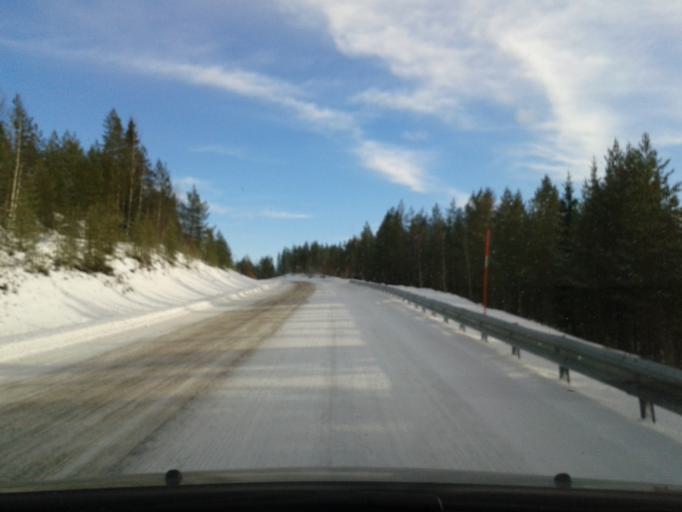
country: SE
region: Vaesterbotten
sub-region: Asele Kommun
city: Asele
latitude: 64.3179
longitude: 17.1255
